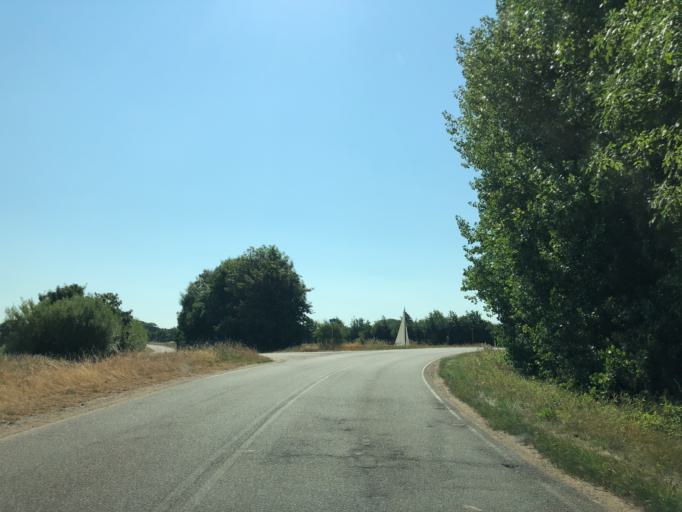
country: DK
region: Zealand
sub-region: Odsherred Kommune
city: Asnaes
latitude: 55.9608
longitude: 11.3896
